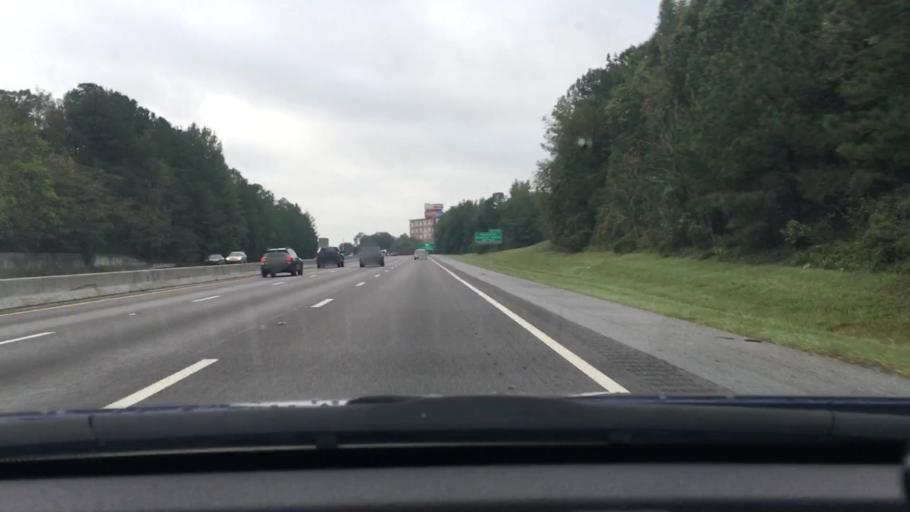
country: US
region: South Carolina
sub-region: Lexington County
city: Saint Andrews
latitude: 34.0127
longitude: -81.1092
